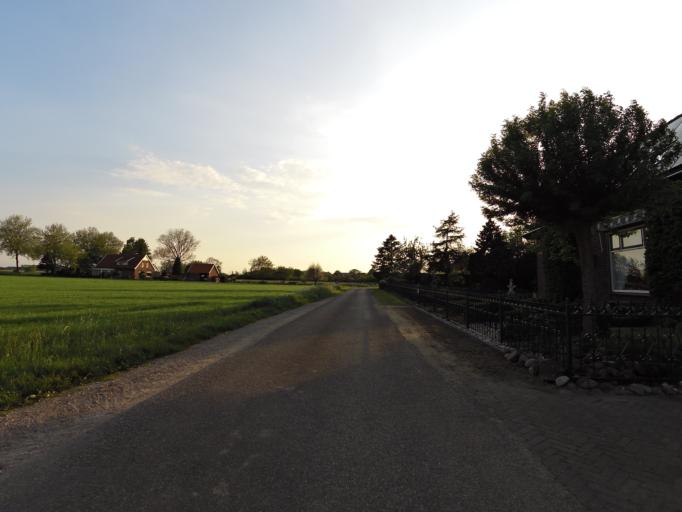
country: NL
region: Gelderland
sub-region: Oude IJsselstreek
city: Gendringen
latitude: 51.8549
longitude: 6.3215
